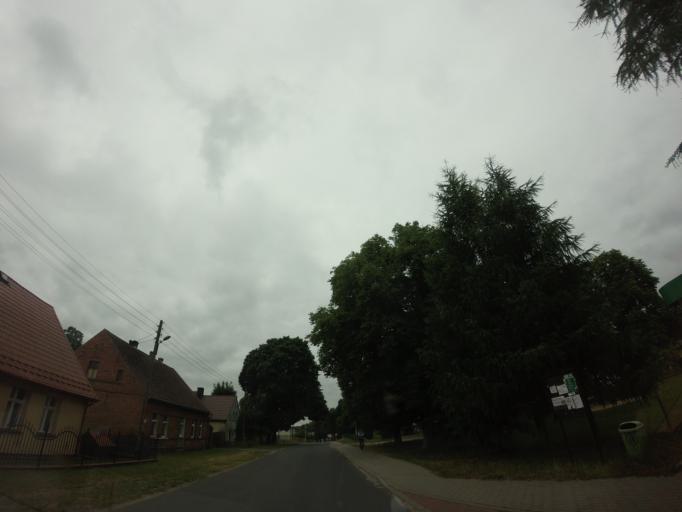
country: PL
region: West Pomeranian Voivodeship
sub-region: Powiat choszczenski
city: Drawno
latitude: 53.1492
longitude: 15.6826
